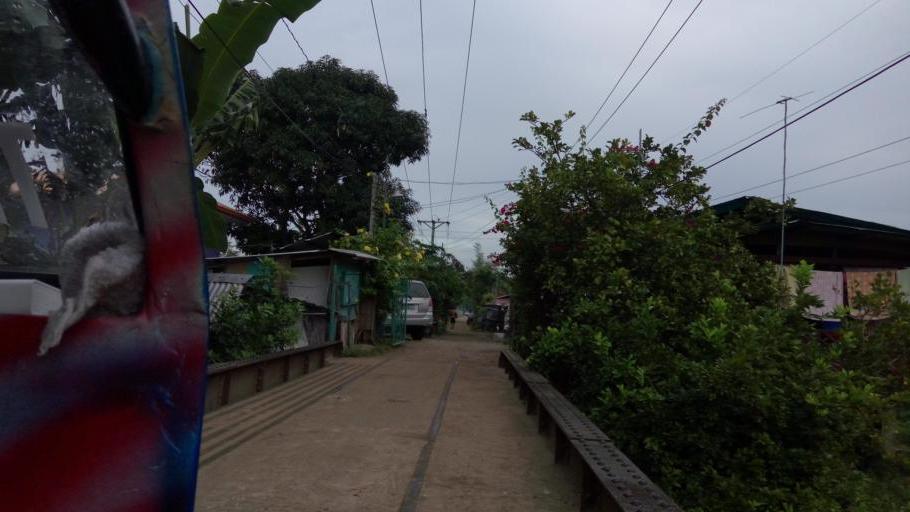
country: PH
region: Ilocos
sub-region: Province of La Union
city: Paringao
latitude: 16.5545
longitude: 120.3255
